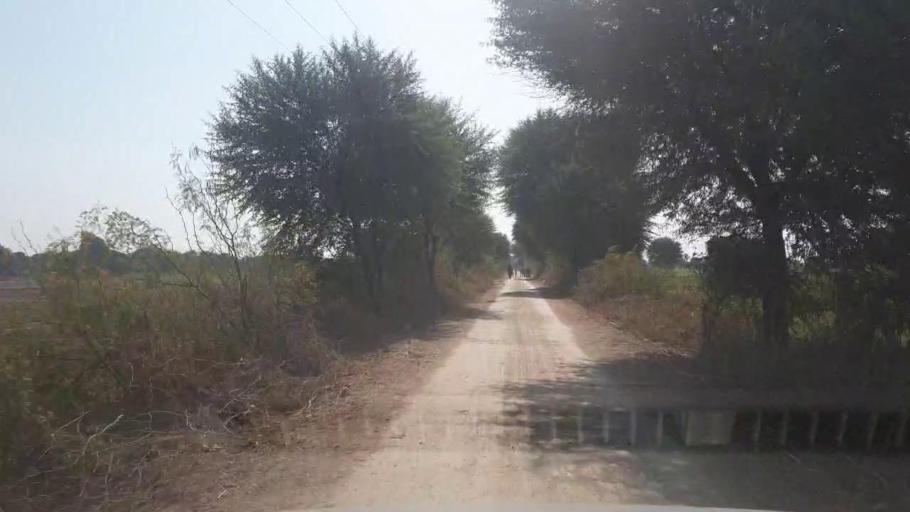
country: PK
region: Sindh
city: Chambar
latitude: 25.2708
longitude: 68.8121
